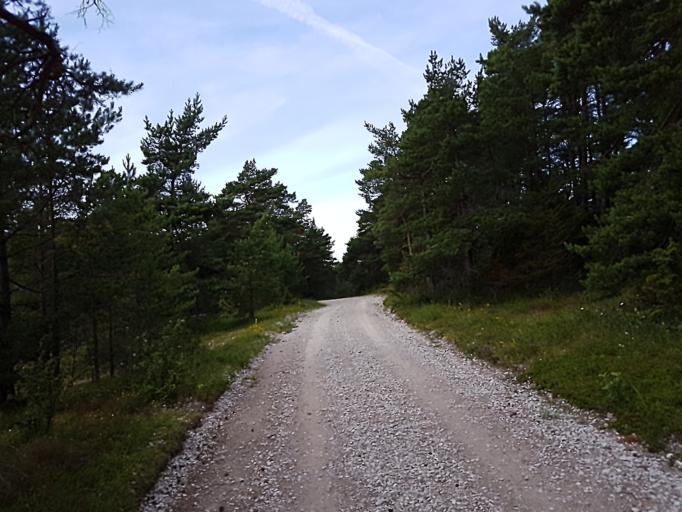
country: SE
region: Gotland
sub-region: Gotland
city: Visby
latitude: 57.6148
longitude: 18.3442
